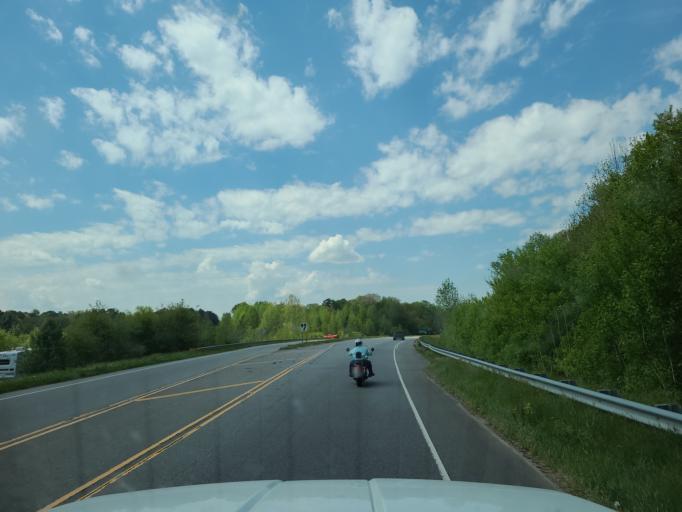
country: US
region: North Carolina
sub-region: Lincoln County
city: Lincolnton
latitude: 35.4275
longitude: -81.2949
